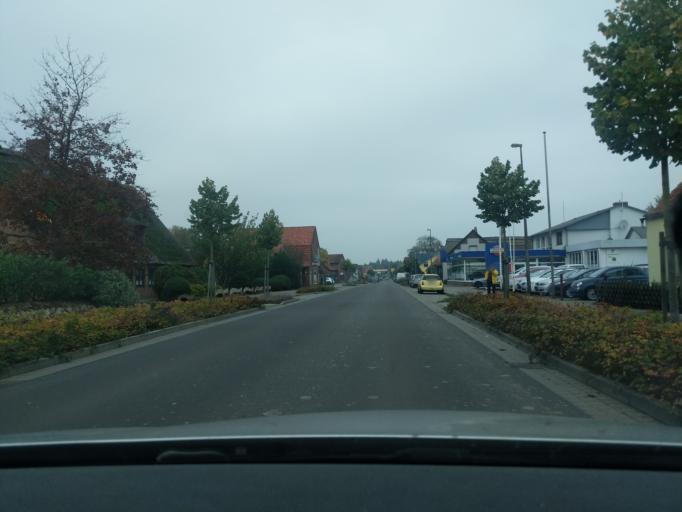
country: DE
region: Lower Saxony
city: Hemmoor
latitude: 53.6788
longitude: 9.1808
